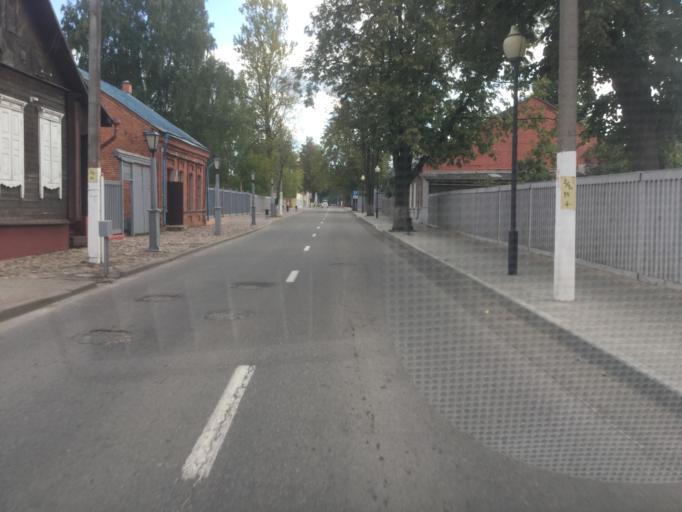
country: BY
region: Vitebsk
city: Vitebsk
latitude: 55.2006
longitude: 30.1904
